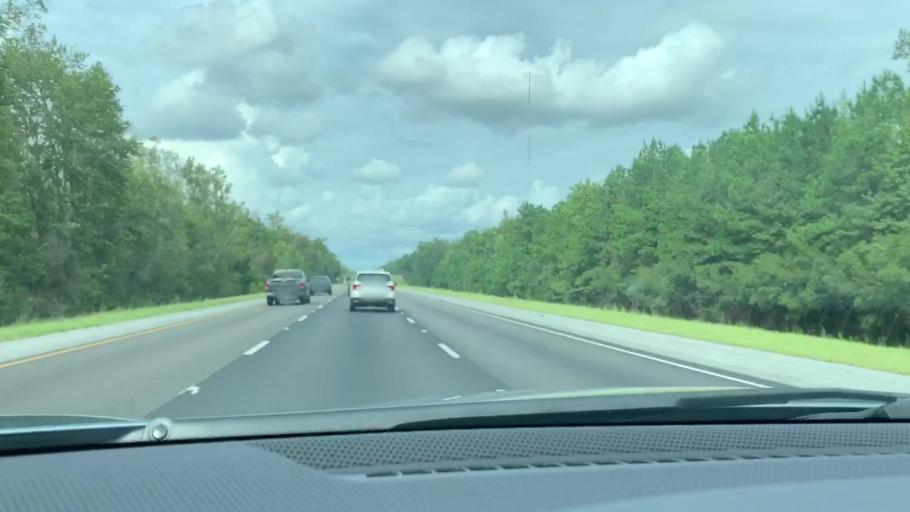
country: US
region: Georgia
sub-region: Liberty County
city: Midway
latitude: 31.6895
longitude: -81.3912
